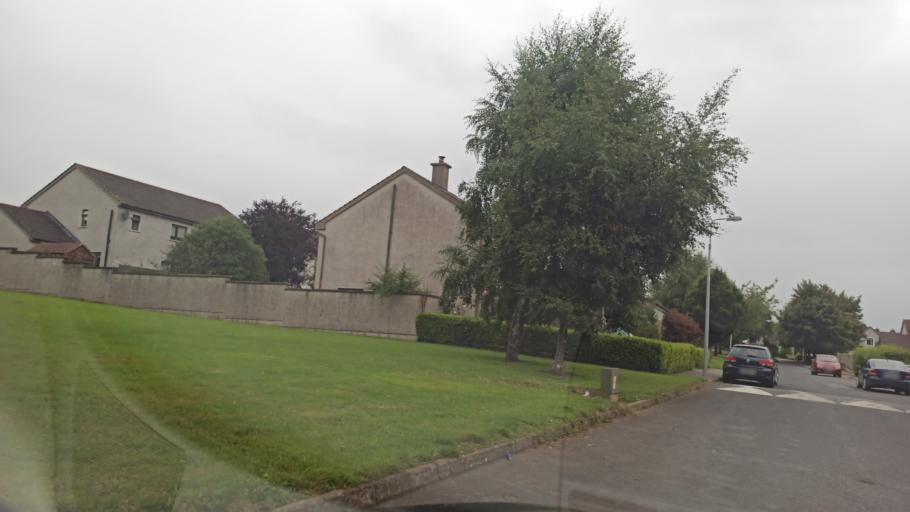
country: IE
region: Munster
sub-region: South Tipperary
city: Cluain Meala
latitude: 52.3656
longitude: -7.7138
